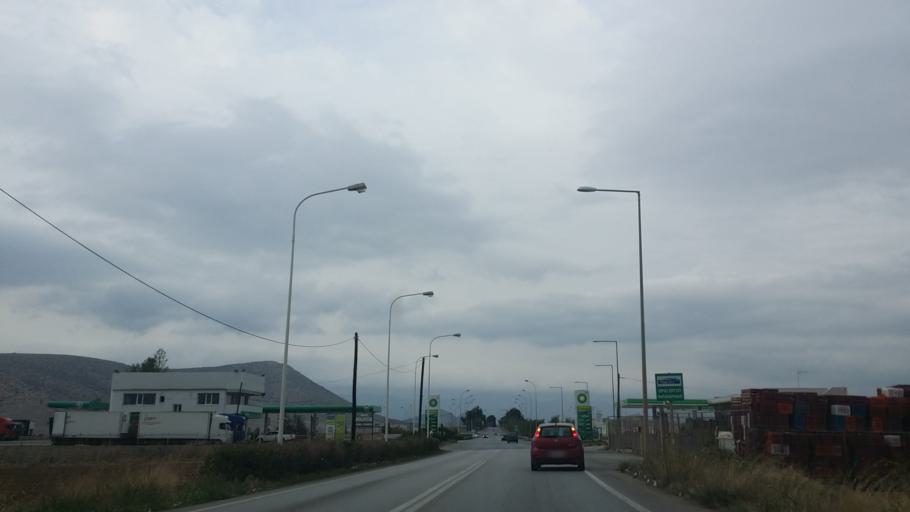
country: GR
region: Central Greece
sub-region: Nomos Voiotias
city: Thivai
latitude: 38.3588
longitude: 23.3221
